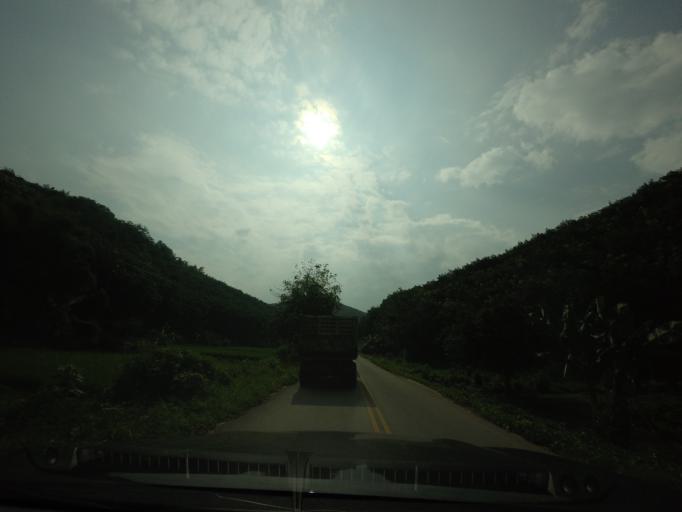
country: TH
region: Loei
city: Chiang Khan
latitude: 17.8328
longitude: 101.5639
